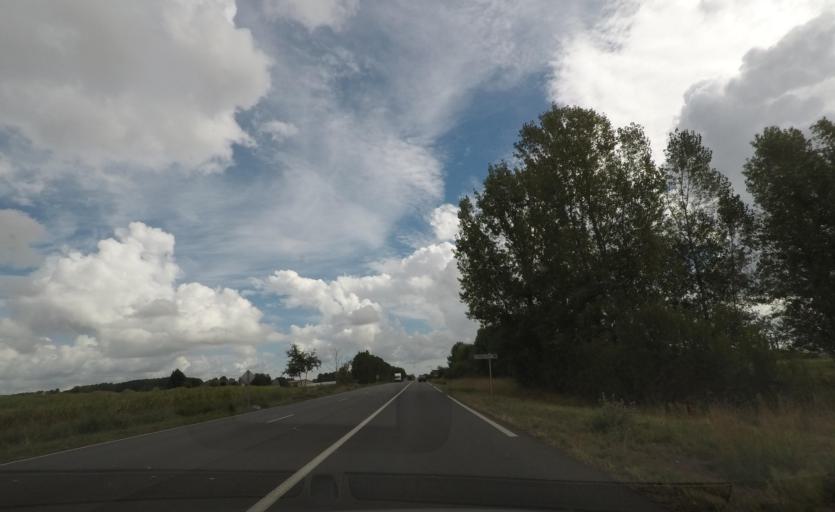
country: FR
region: Pays de la Loire
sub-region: Departement de Maine-et-Loire
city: Corze
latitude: 47.5443
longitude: -0.3975
